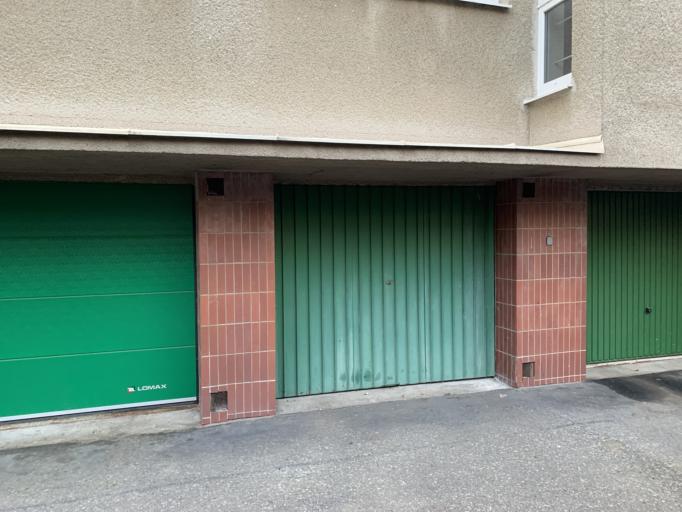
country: CZ
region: Praha
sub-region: Praha 9
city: Vysocany
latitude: 50.0707
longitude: 14.4979
